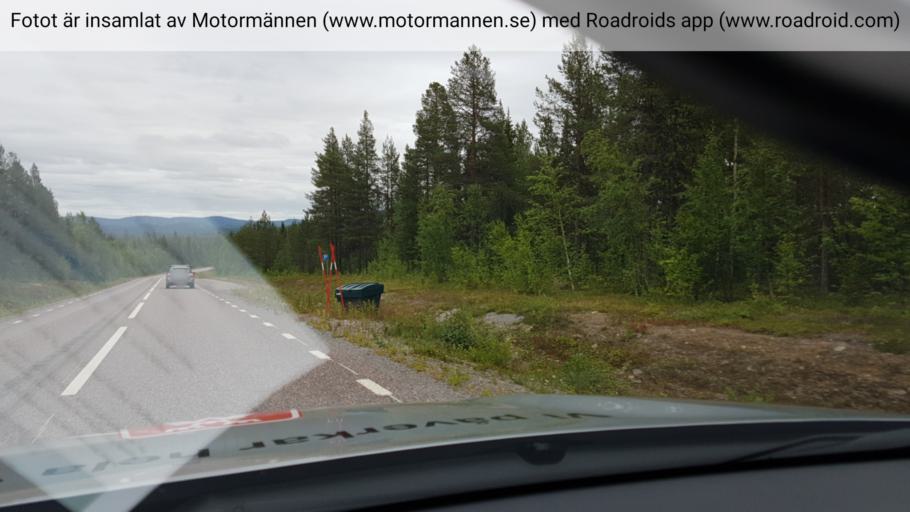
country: SE
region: Norrbotten
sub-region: Gallivare Kommun
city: Gaellivare
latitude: 67.0342
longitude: 21.6959
